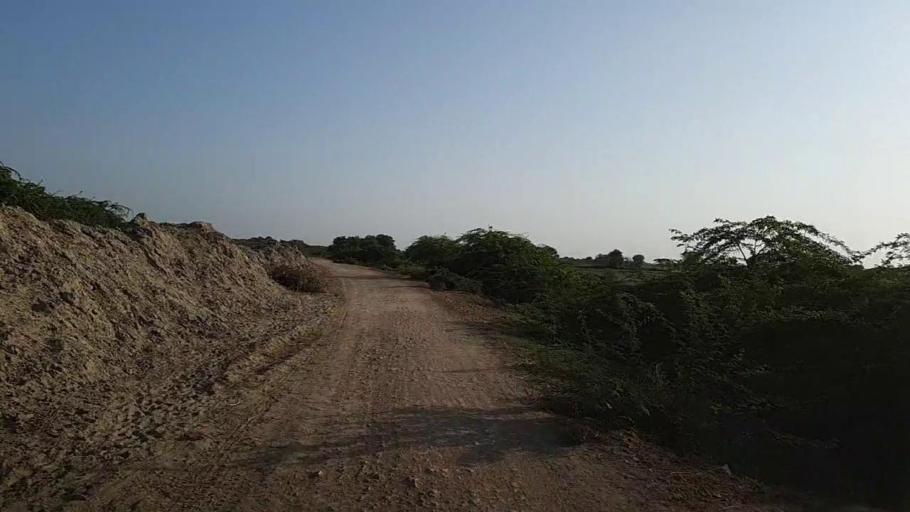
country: PK
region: Sindh
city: Kario
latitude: 24.7383
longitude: 68.6695
